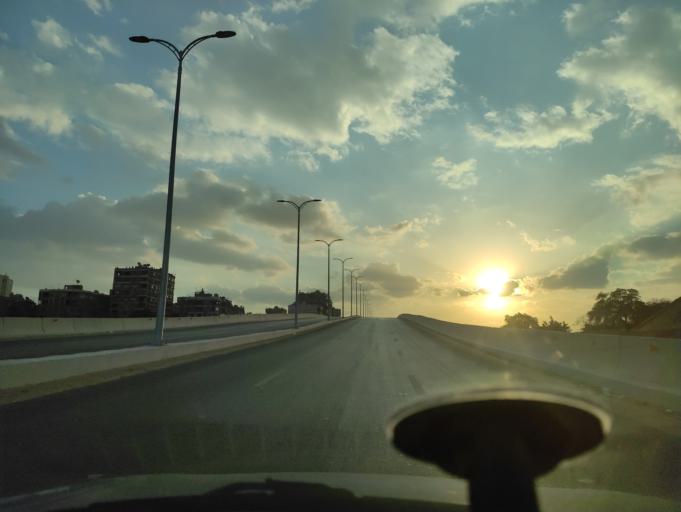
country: EG
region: Muhafazat al Qalyubiyah
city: Al Khankah
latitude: 30.1211
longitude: 31.3531
